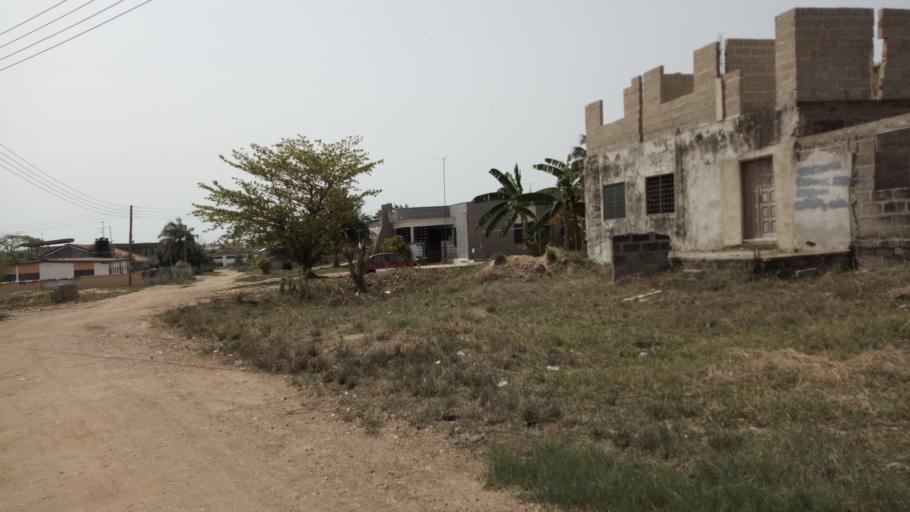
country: GH
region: Central
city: Winneba
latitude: 5.3677
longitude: -0.6445
